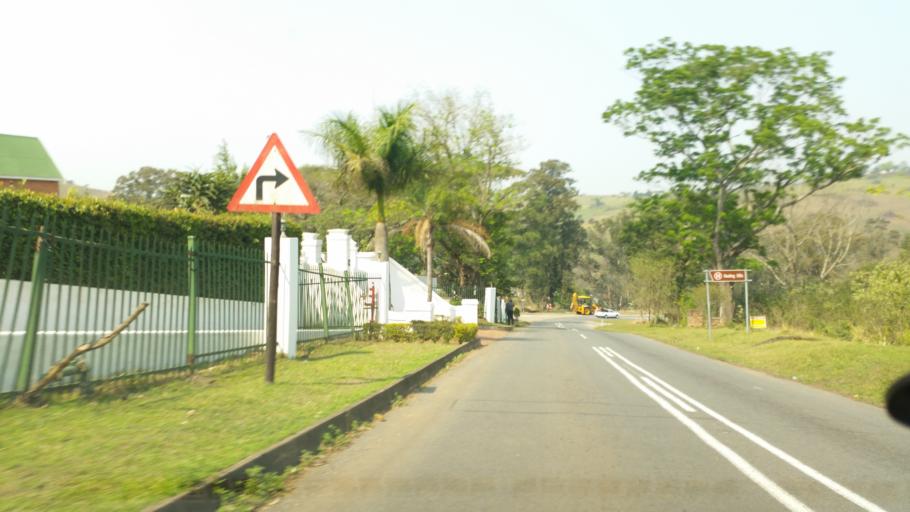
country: ZA
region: KwaZulu-Natal
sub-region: eThekwini Metropolitan Municipality
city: Mpumalanga
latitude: -29.7391
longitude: 30.6635
